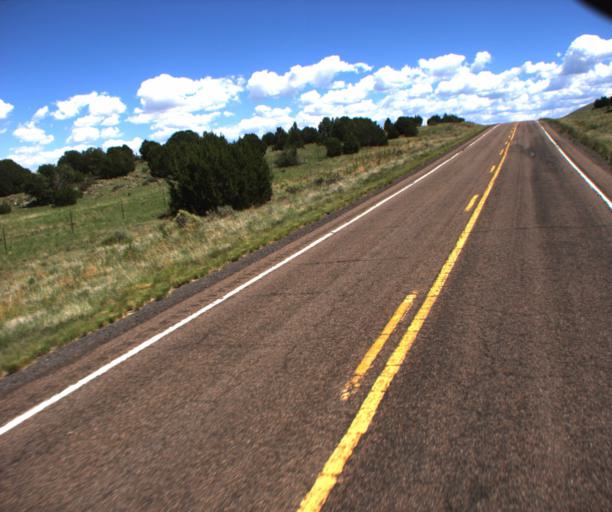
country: US
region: Arizona
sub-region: Apache County
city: Springerville
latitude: 34.2542
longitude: -109.5438
